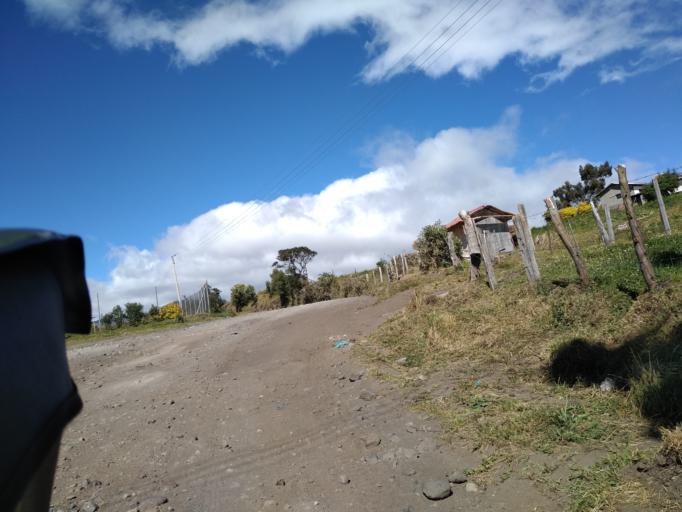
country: EC
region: Pichincha
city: Machachi
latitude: -0.5329
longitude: -78.4833
